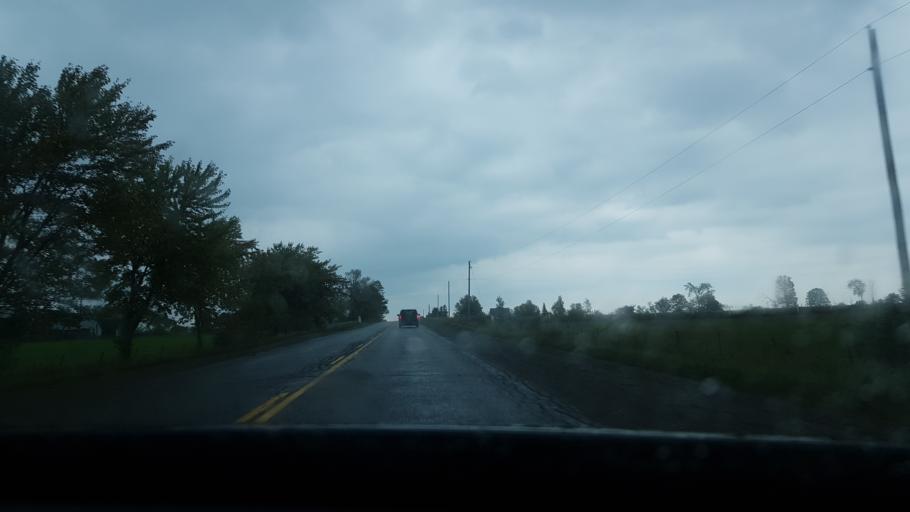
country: CA
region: Ontario
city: Omemee
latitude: 44.3802
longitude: -78.6165
